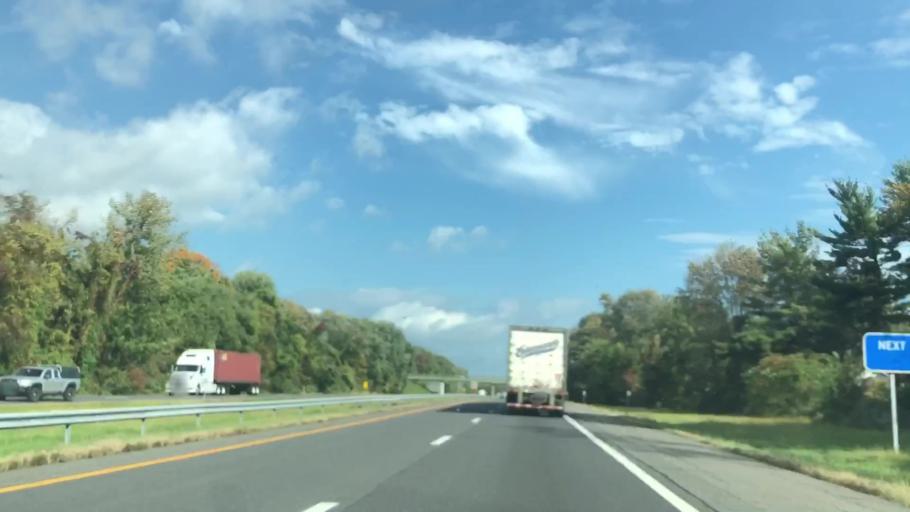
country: US
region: New York
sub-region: Ulster County
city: Glasco
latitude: 42.0363
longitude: -73.9901
